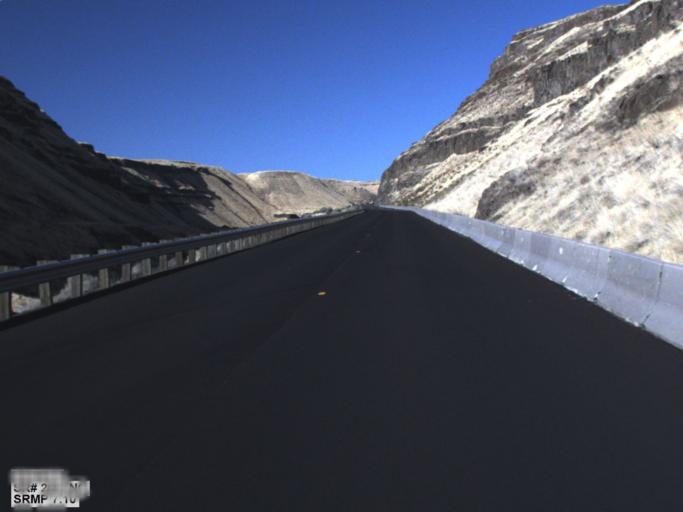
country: US
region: Washington
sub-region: Franklin County
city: Connell
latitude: 46.6163
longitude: -118.5565
